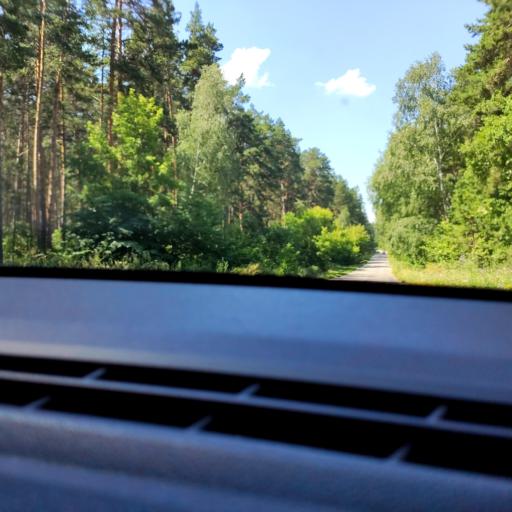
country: RU
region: Samara
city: Podstepki
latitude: 53.5721
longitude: 49.0355
